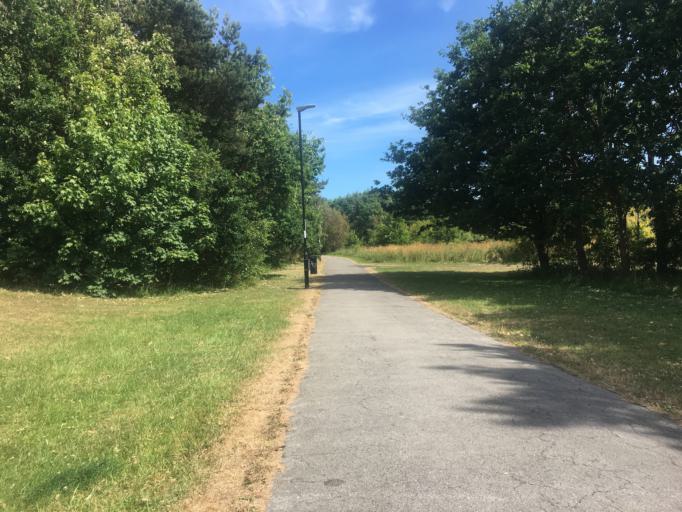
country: GB
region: England
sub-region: County Durham
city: Chester-le-Street
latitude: 54.8783
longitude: -1.5483
